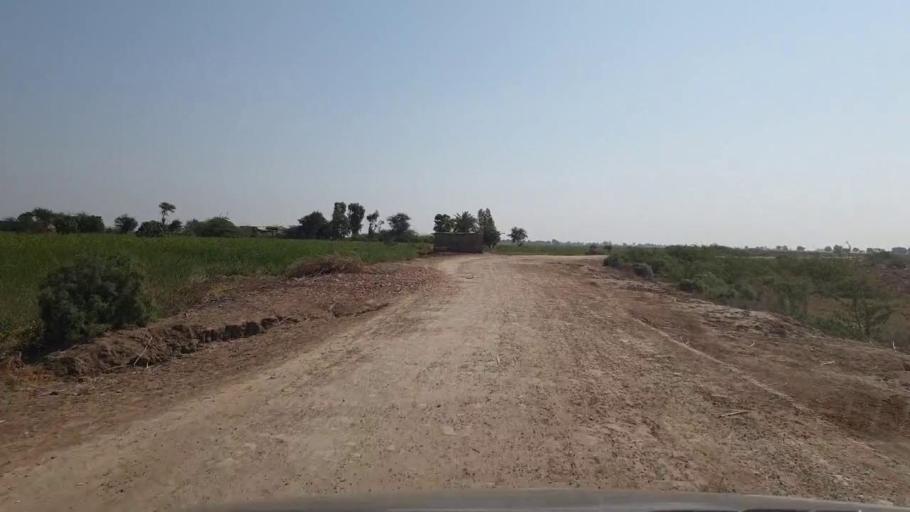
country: PK
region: Sindh
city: Samaro
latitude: 25.2419
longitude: 69.2871
